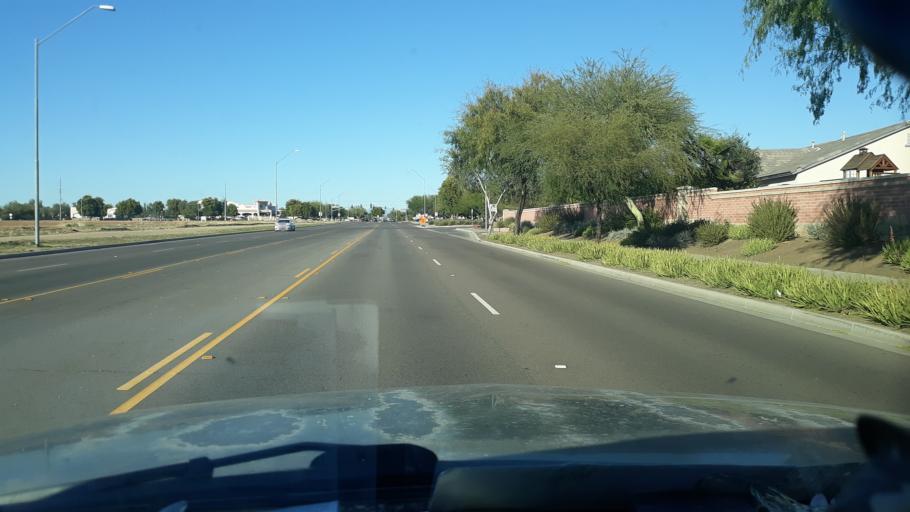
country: US
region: Arizona
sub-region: Maricopa County
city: Surprise
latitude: 33.6066
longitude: -112.3938
